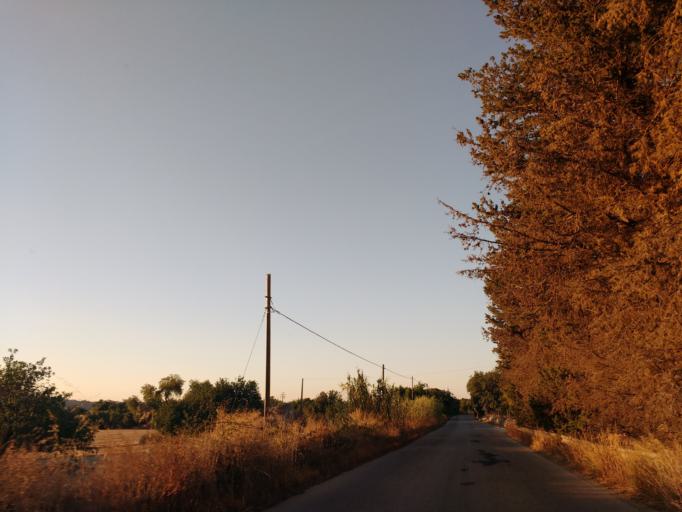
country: IT
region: Sicily
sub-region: Ragusa
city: Ispica
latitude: 36.7598
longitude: 14.9234
